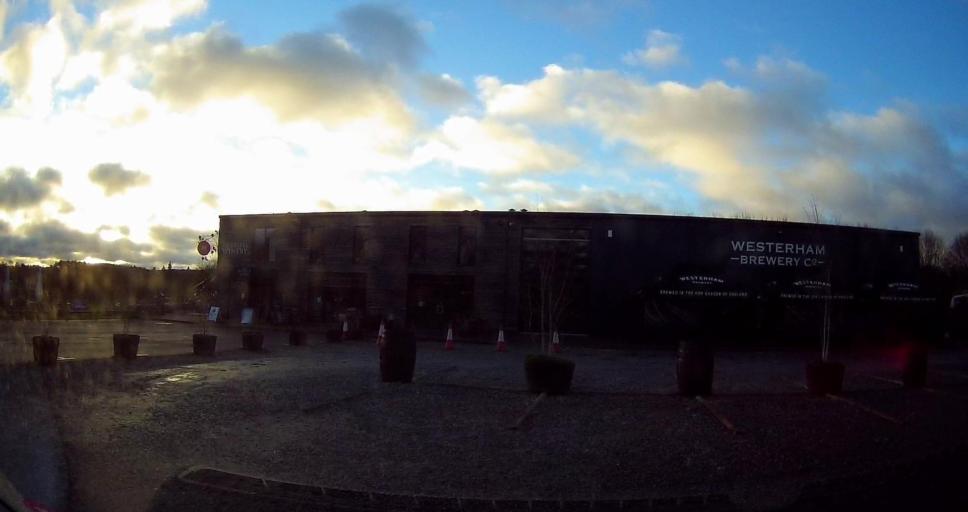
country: GB
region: England
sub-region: Kent
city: Westerham
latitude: 51.2763
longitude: 0.0853
